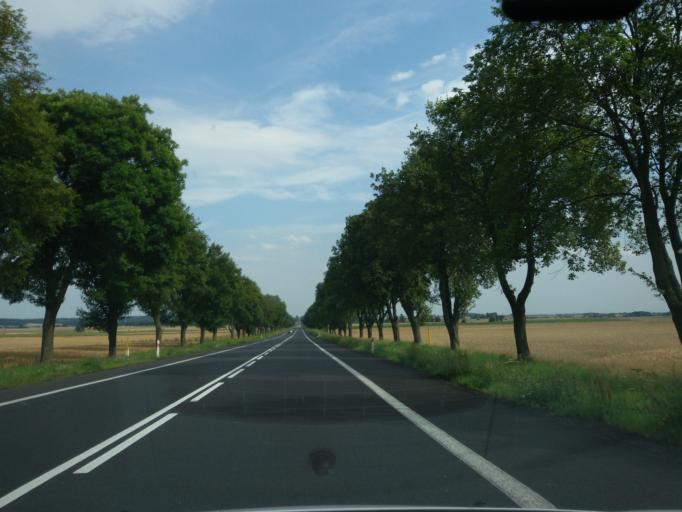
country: PL
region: Lower Silesian Voivodeship
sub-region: Powiat polkowicki
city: Gaworzyce
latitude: 51.6287
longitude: 15.9092
